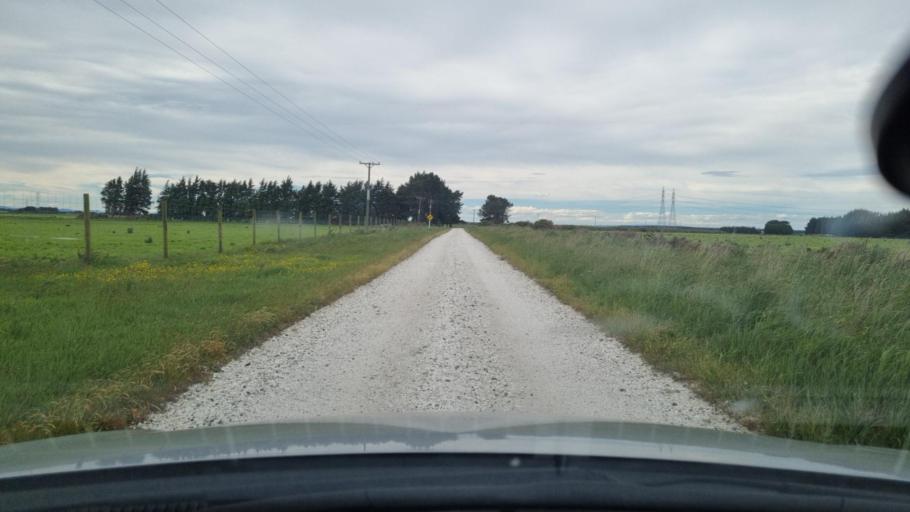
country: NZ
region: Southland
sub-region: Invercargill City
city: Invercargill
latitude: -46.4933
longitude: 168.4255
